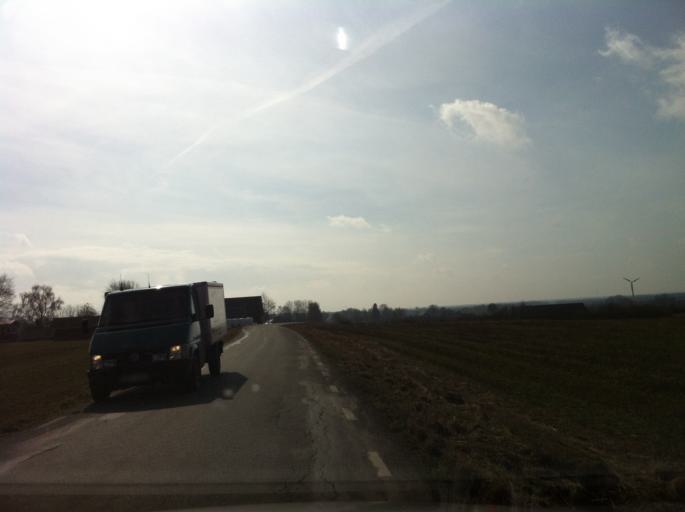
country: SE
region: Vaestra Goetaland
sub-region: Falkopings Kommun
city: Falkoeping
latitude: 58.2156
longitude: 13.4627
